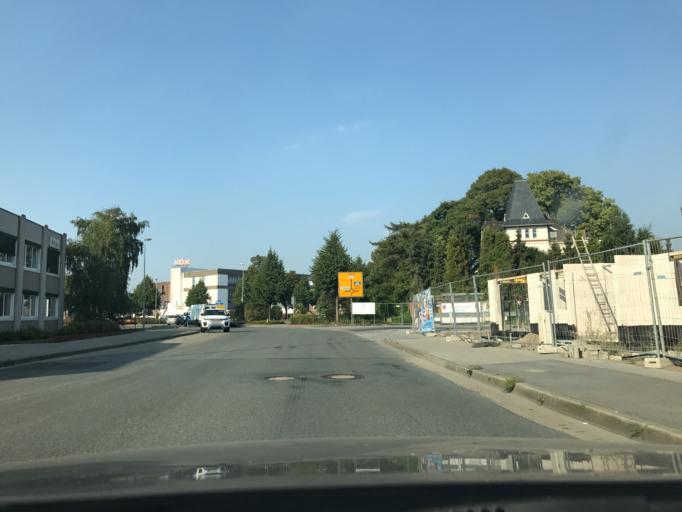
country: DE
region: North Rhine-Westphalia
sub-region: Regierungsbezirk Dusseldorf
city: Kleve
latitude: 51.7924
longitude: 6.1457
